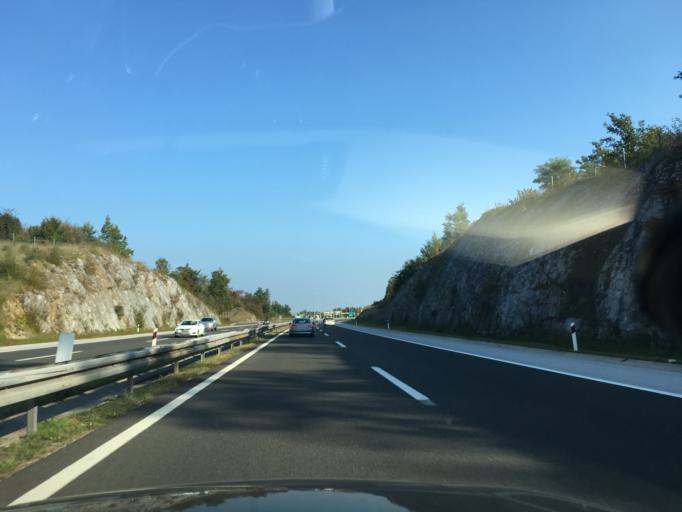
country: HR
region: Karlovacka
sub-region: Grad Ogulin
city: Ogulin
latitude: 45.3026
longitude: 15.2789
